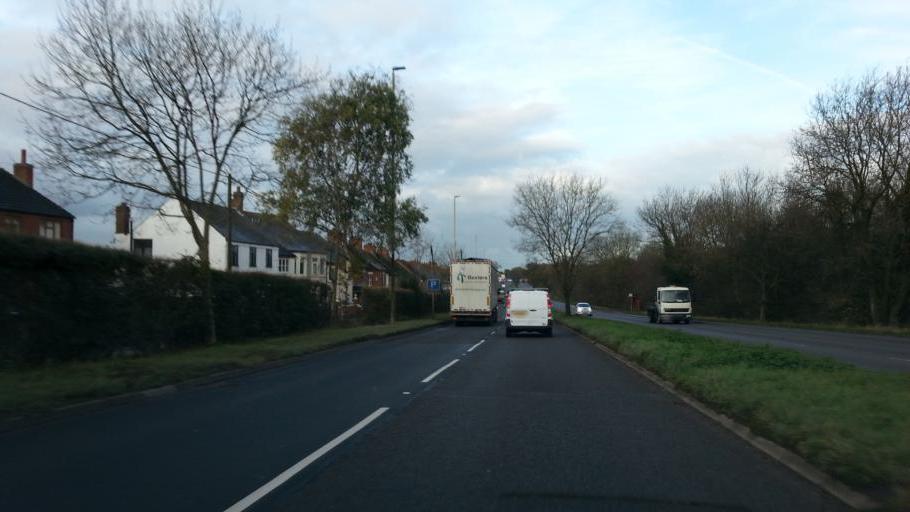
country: GB
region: England
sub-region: Leicestershire
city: Markfield
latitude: 52.7016
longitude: -1.3137
